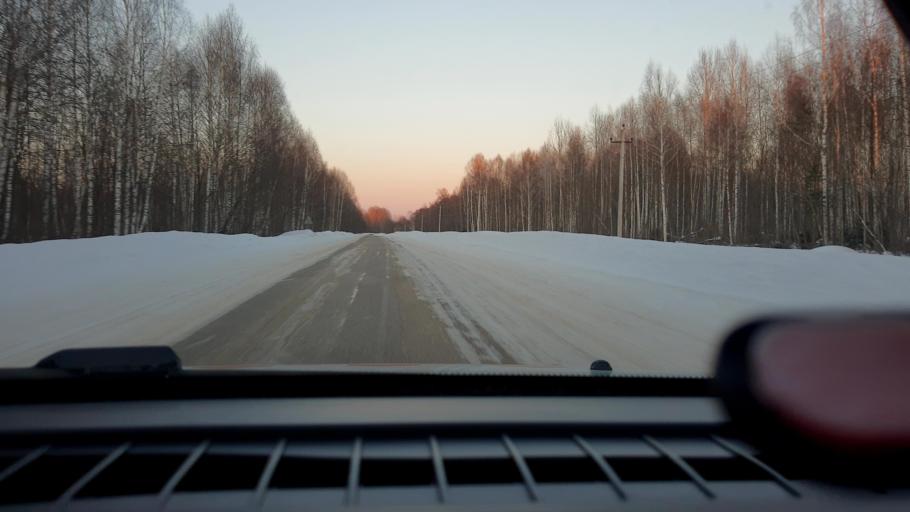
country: RU
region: Nizjnij Novgorod
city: Lyskovo
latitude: 56.1581
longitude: 45.1604
